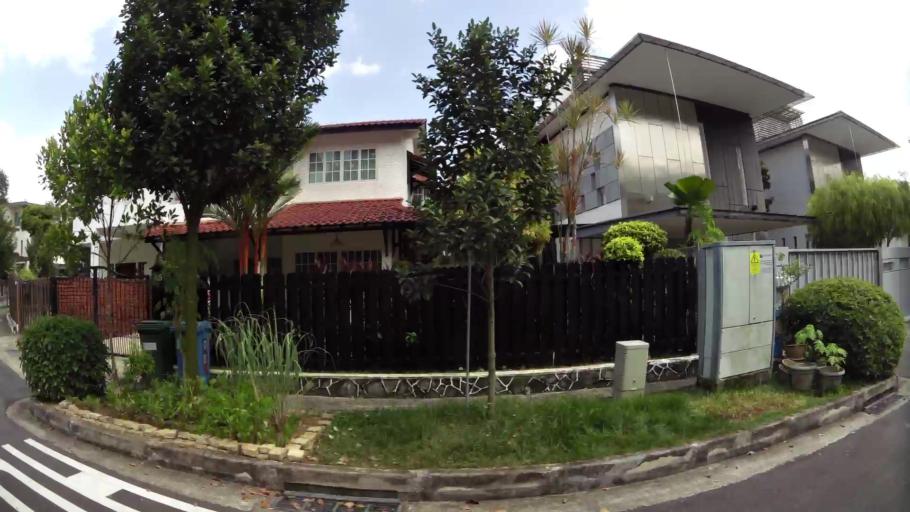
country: SG
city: Singapore
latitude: 1.3501
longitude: 103.8326
